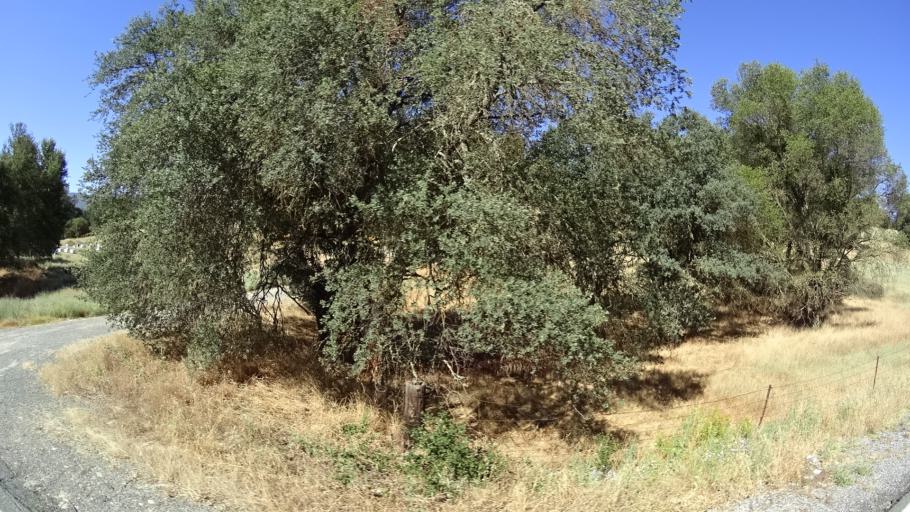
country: US
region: California
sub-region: Calaveras County
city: San Andreas
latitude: 38.2143
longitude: -120.6878
